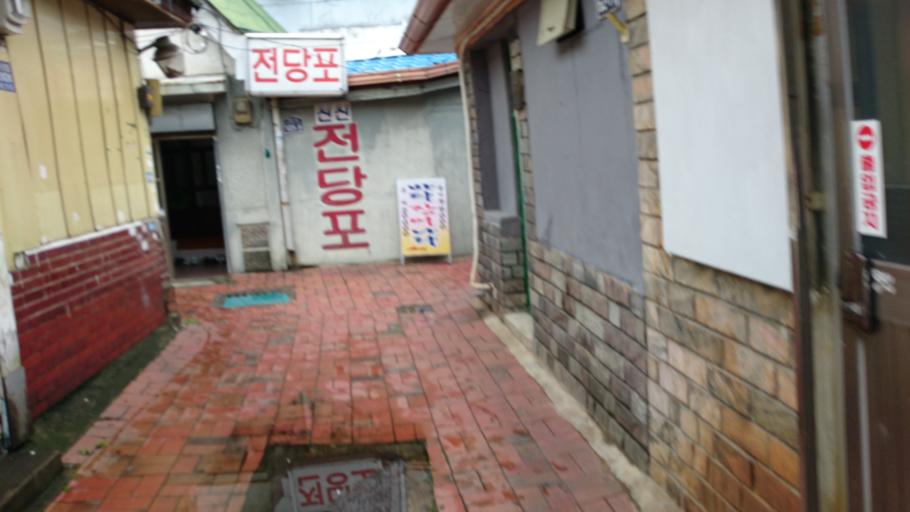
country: KR
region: Daegu
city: Daegu
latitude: 35.8735
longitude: 128.5935
